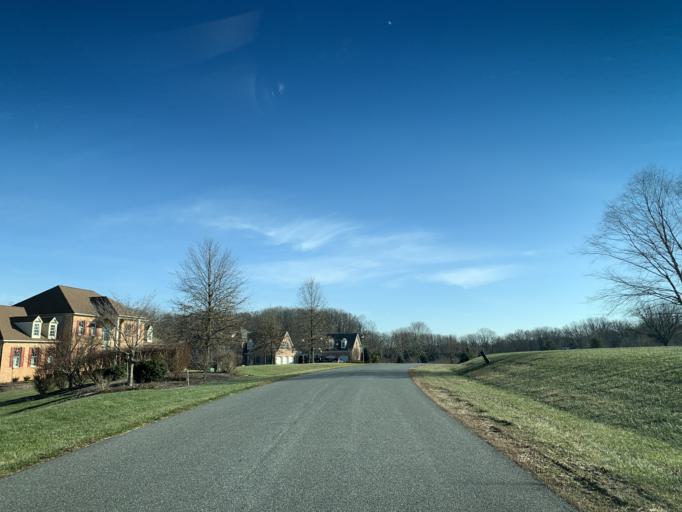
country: US
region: Maryland
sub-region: Harford County
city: South Bel Air
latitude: 39.5689
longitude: -76.2522
